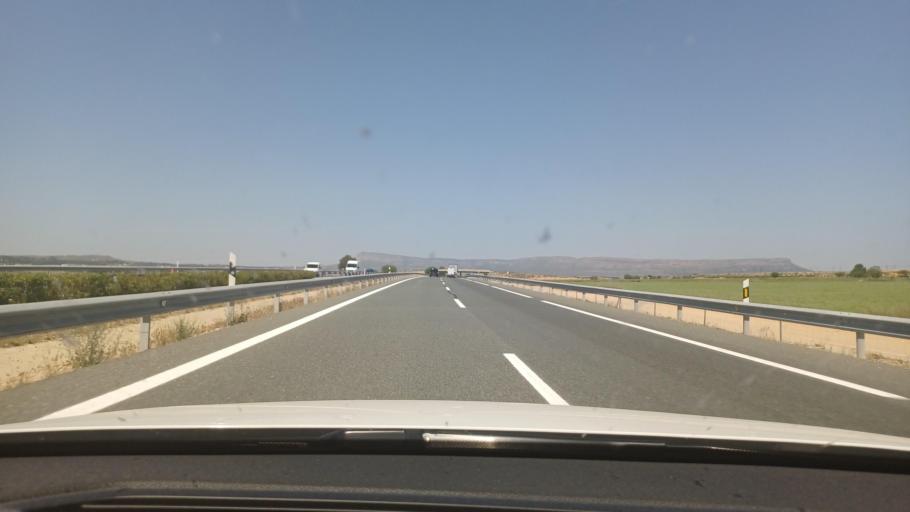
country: ES
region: Castille-La Mancha
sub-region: Provincia de Albacete
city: Almansa
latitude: 38.8614
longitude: -1.0414
